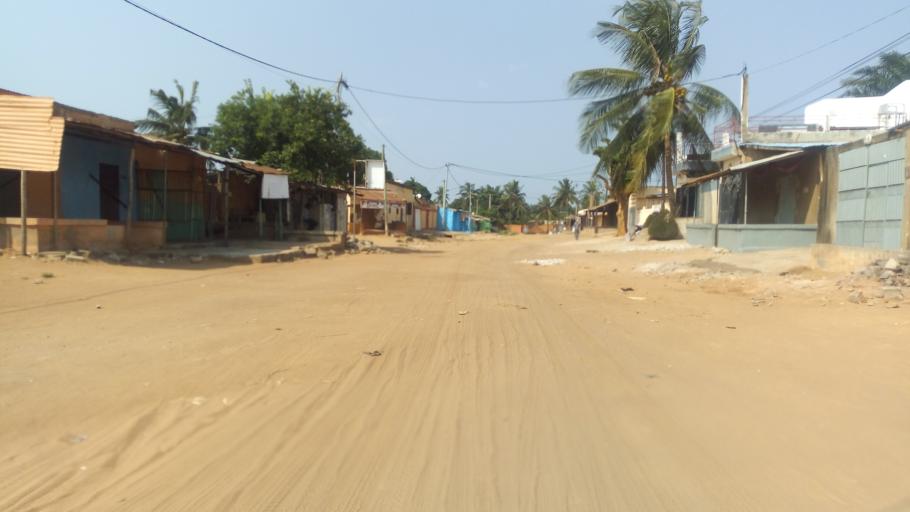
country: TG
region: Maritime
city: Lome
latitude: 6.1901
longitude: 1.1816
